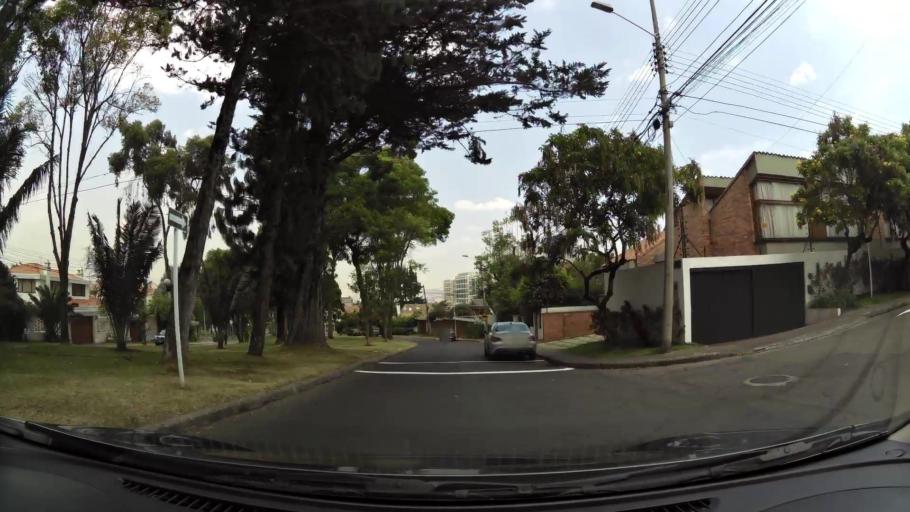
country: CO
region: Bogota D.C.
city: Barrio San Luis
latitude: 4.6874
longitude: -74.0308
